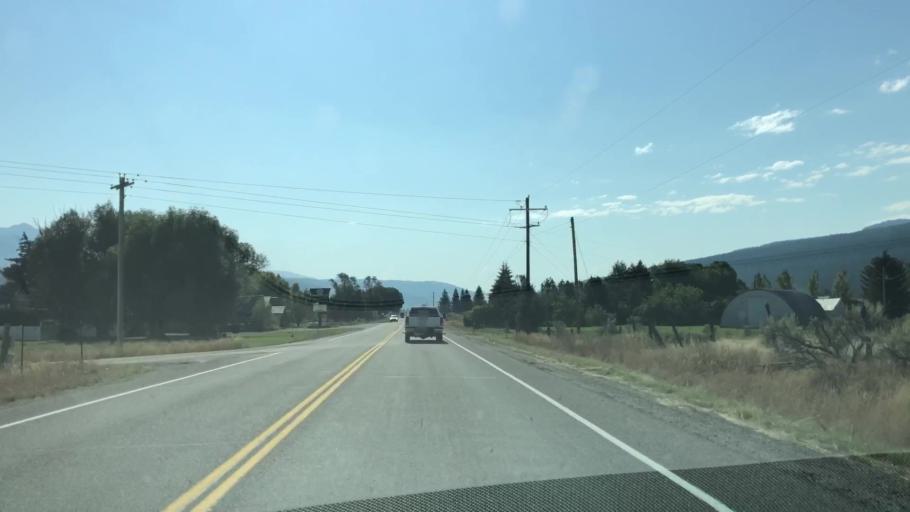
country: US
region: Idaho
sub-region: Teton County
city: Victor
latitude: 43.4028
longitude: -111.2904
